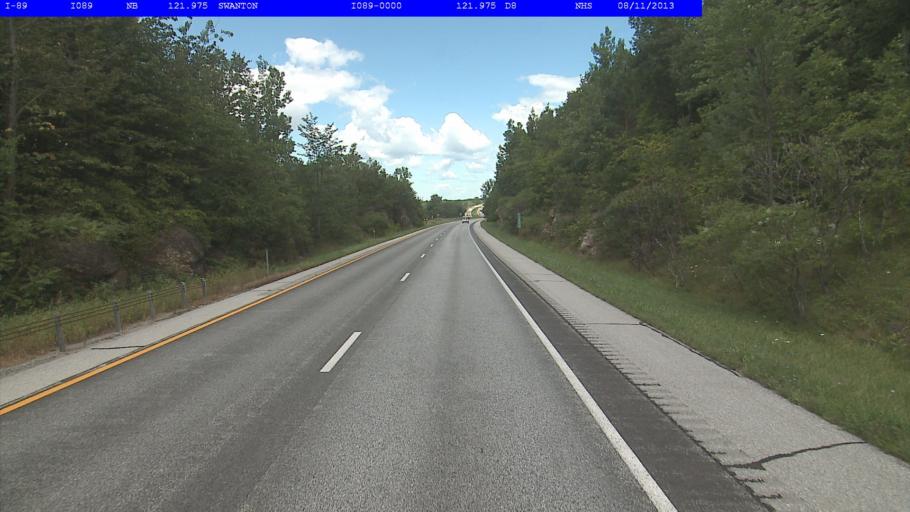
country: US
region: Vermont
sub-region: Franklin County
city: Swanton
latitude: 44.9037
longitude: -73.0962
